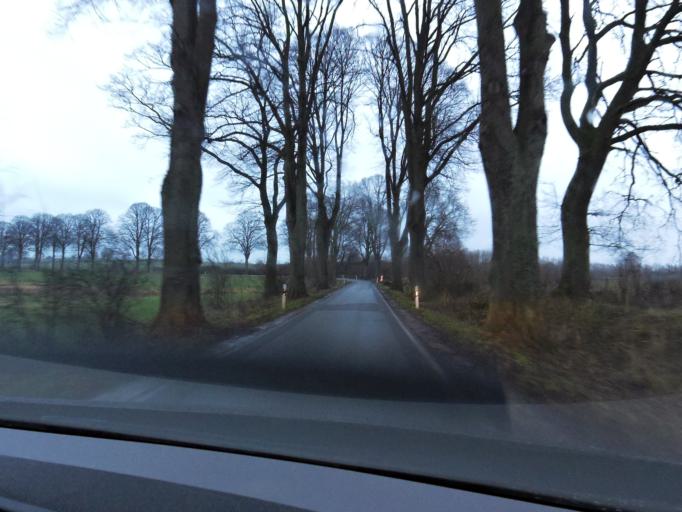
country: DE
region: Schleswig-Holstein
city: Kittlitz
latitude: 53.6600
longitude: 10.8997
